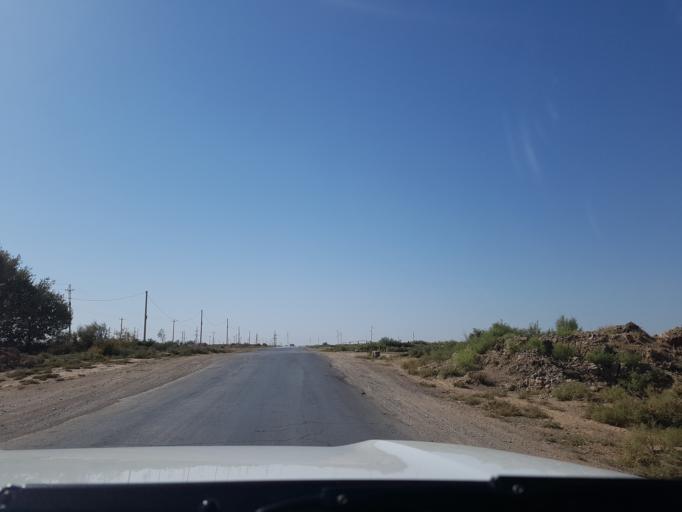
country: IR
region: Razavi Khorasan
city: Sarakhs
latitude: 36.5217
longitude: 61.2451
